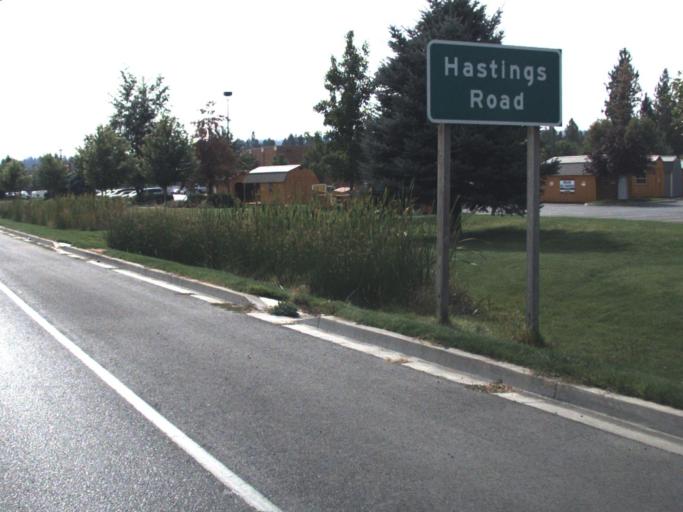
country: US
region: Washington
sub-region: Spokane County
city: Fairwood
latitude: 47.7708
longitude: -117.4039
